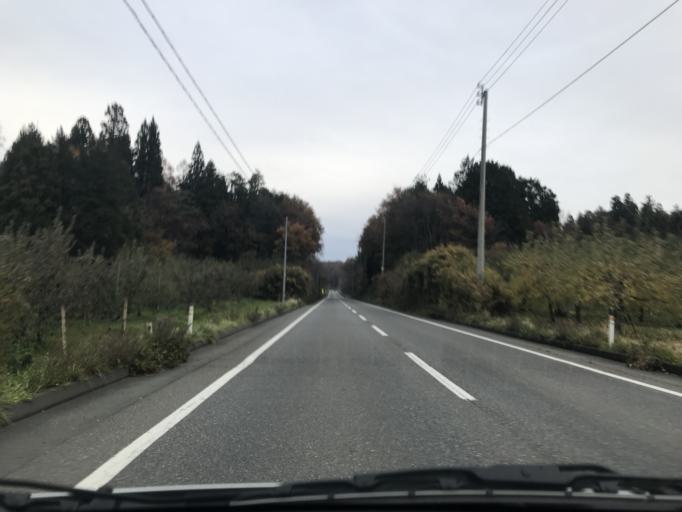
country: JP
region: Iwate
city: Kitakami
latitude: 39.2864
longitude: 141.2254
